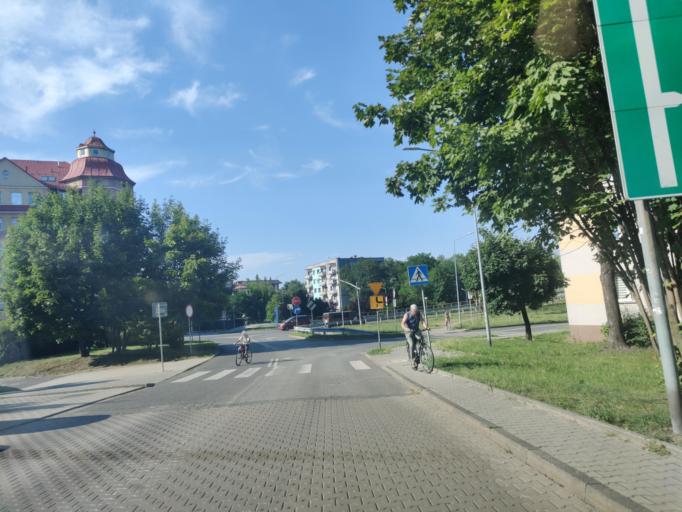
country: PL
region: Silesian Voivodeship
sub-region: Myslowice
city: Myslowice
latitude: 50.2423
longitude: 19.1418
